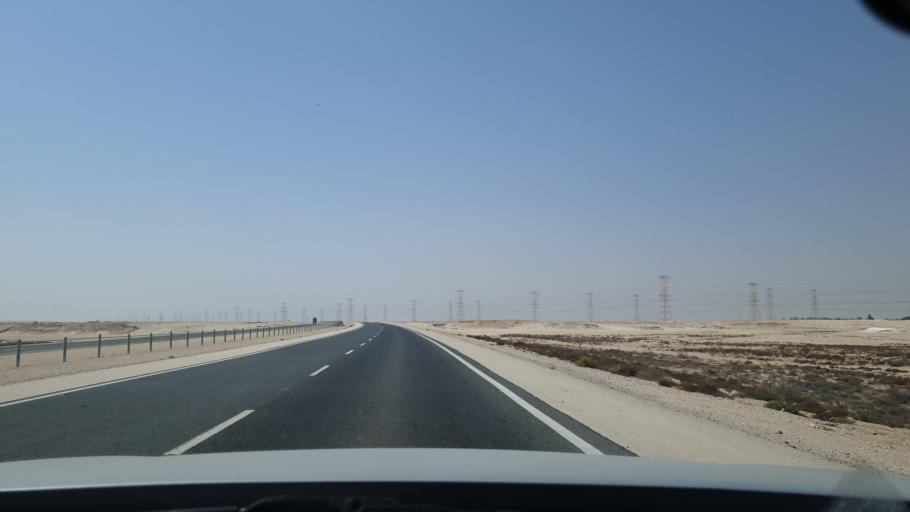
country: QA
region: Al Khawr
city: Al Khawr
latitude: 25.7506
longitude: 51.4697
